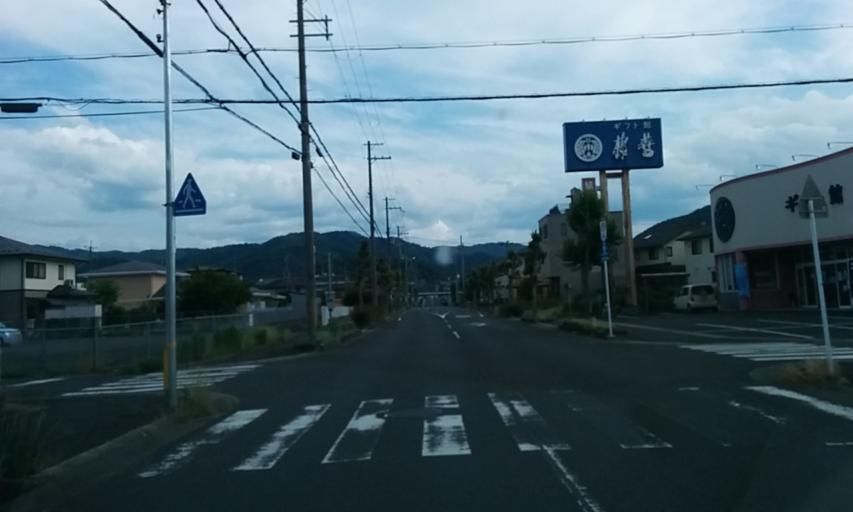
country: JP
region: Kyoto
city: Ayabe
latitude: 35.3040
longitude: 135.2621
